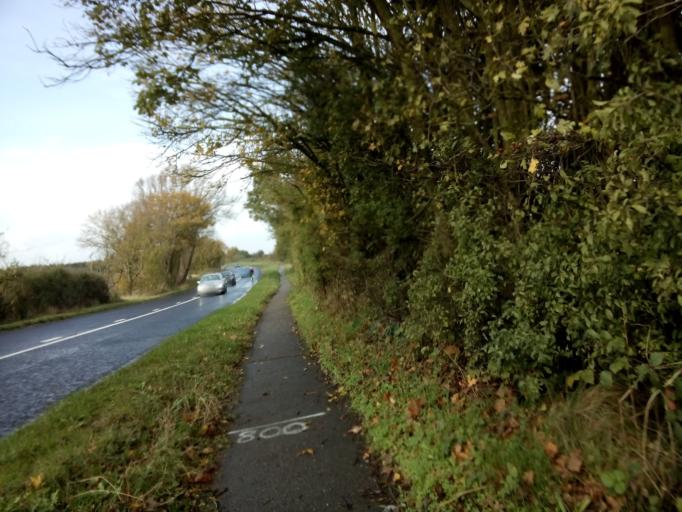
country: GB
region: England
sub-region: Suffolk
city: Needham Market
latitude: 52.1647
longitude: 1.0348
